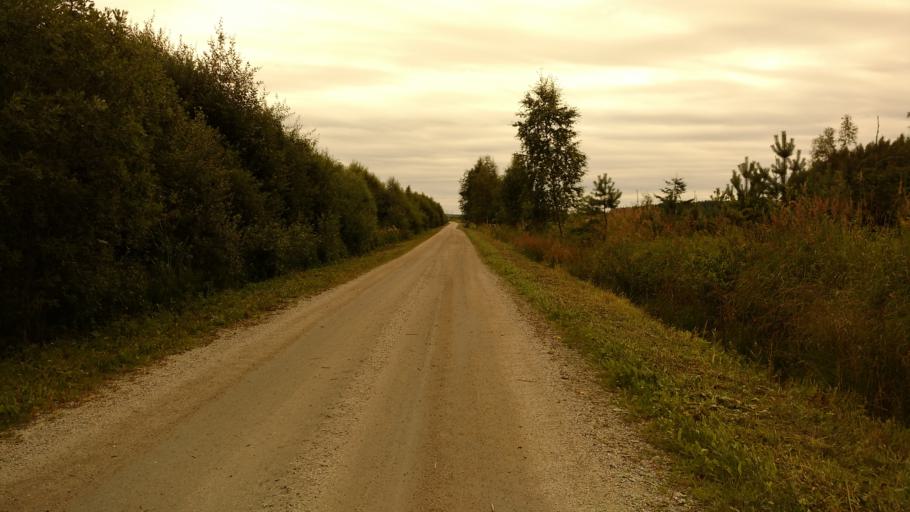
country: FI
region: Varsinais-Suomi
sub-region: Turku
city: Paimio
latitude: 60.4251
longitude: 22.8032
